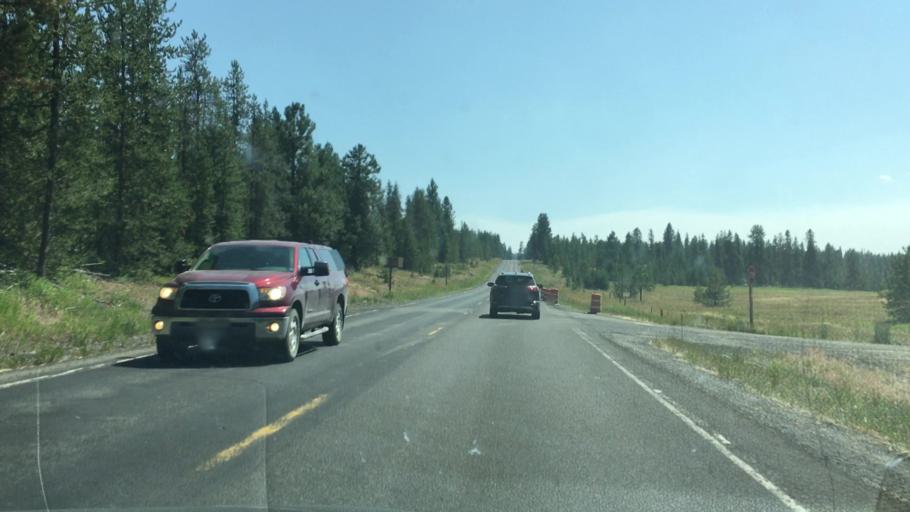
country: US
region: Idaho
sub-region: Valley County
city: McCall
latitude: 44.9548
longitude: -116.1698
